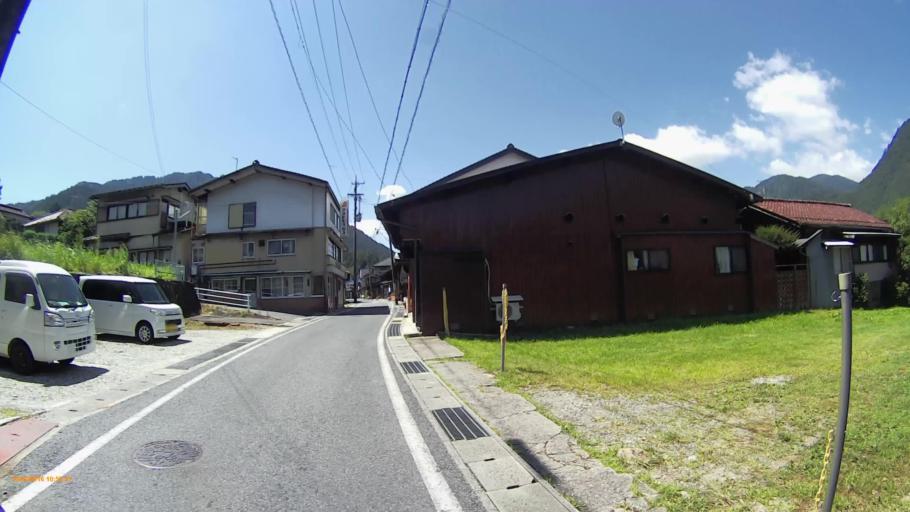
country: JP
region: Gifu
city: Nakatsugawa
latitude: 35.6725
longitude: 137.6369
